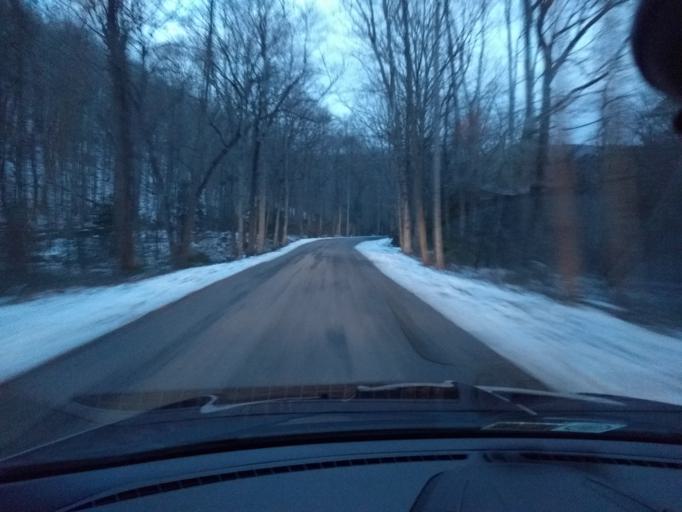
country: US
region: Virginia
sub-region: Alleghany County
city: Clifton Forge
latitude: 37.8564
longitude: -79.8623
